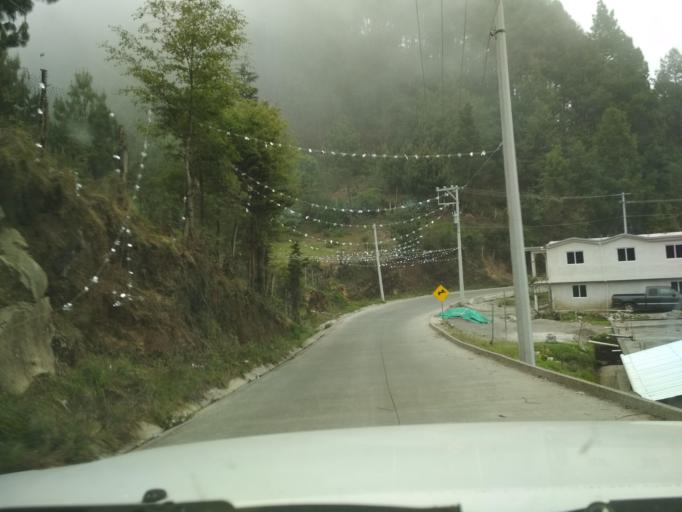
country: MX
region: Veracruz
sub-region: La Perla
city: Chilapa
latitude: 18.9773
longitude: -97.1907
